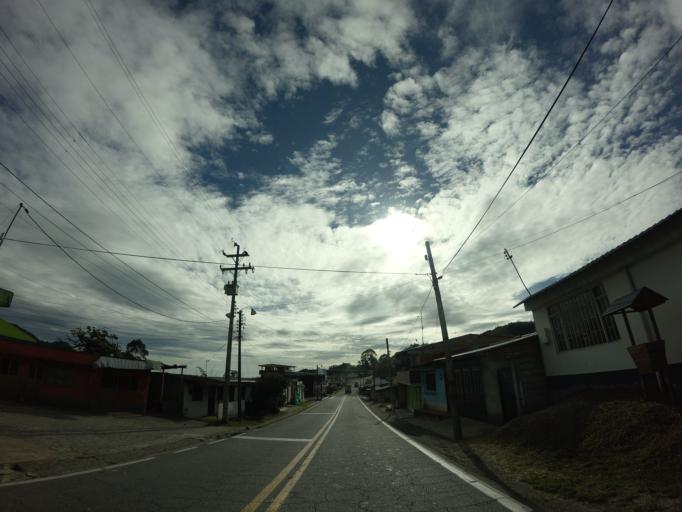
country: CO
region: Tolima
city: Herveo
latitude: 5.1349
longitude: -75.1405
